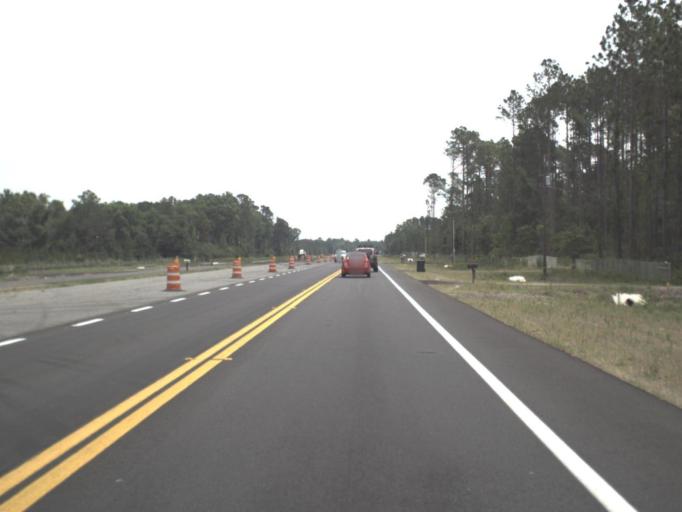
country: US
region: Florida
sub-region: Nassau County
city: Nassau Village-Ratliff
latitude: 30.4635
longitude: -81.9107
